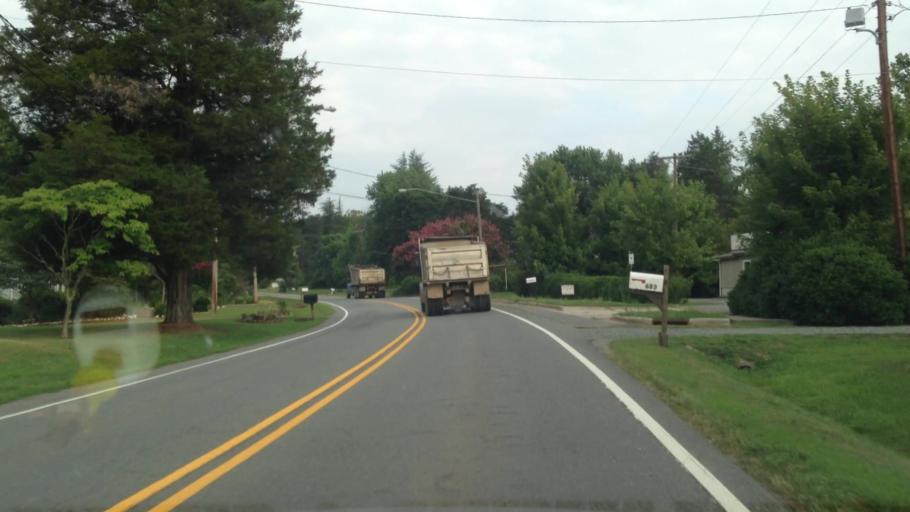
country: US
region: North Carolina
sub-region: Forsyth County
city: Rural Hall
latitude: 36.1935
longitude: -80.2491
